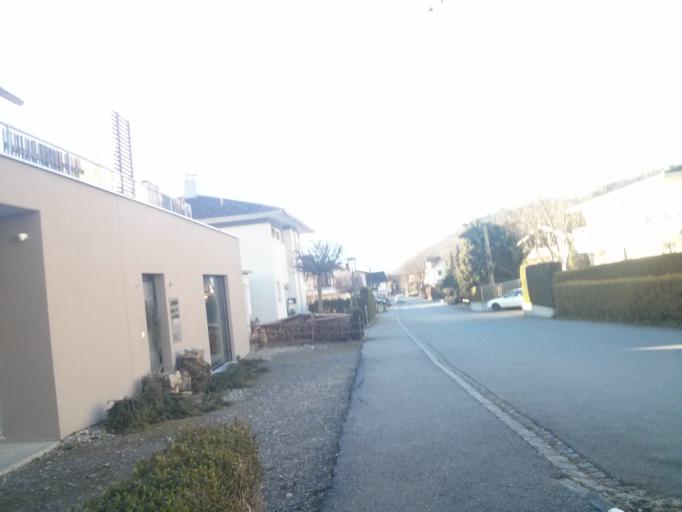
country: AT
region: Vorarlberg
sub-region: Politischer Bezirk Feldkirch
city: Klaus
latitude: 47.3102
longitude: 9.6459
